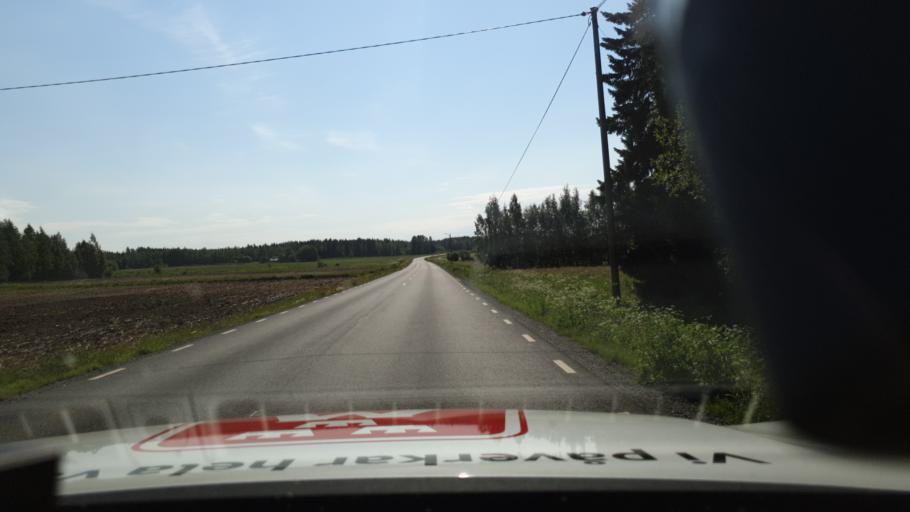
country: SE
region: Norrbotten
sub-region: Lulea Kommun
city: Gammelstad
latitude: 65.7986
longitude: 22.0602
